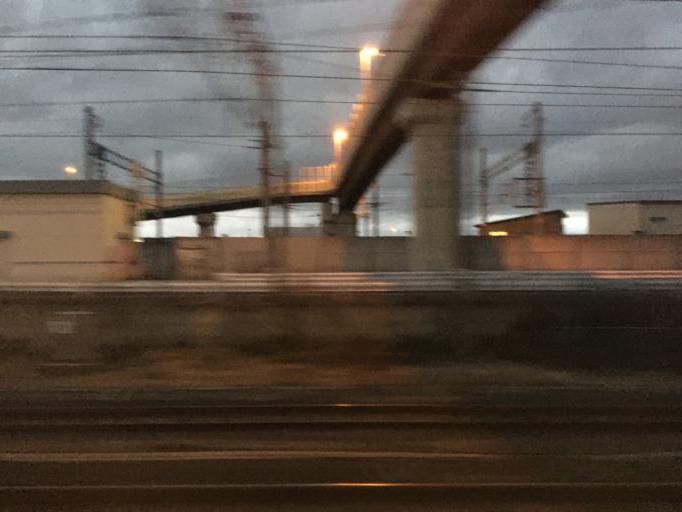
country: JP
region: Aomori
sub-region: Hachinohe Shi
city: Uchimaru
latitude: 40.5129
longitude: 141.4350
